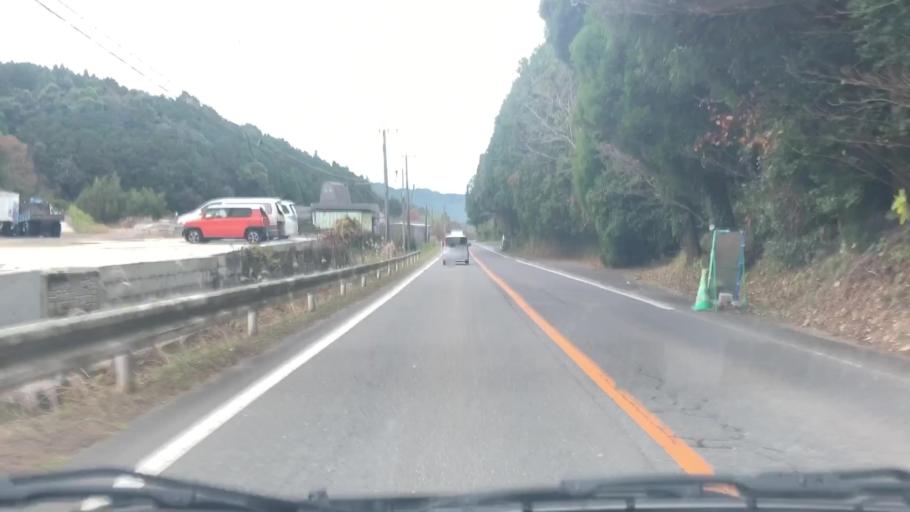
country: JP
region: Saga Prefecture
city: Takeocho-takeo
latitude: 33.1842
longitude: 129.9693
